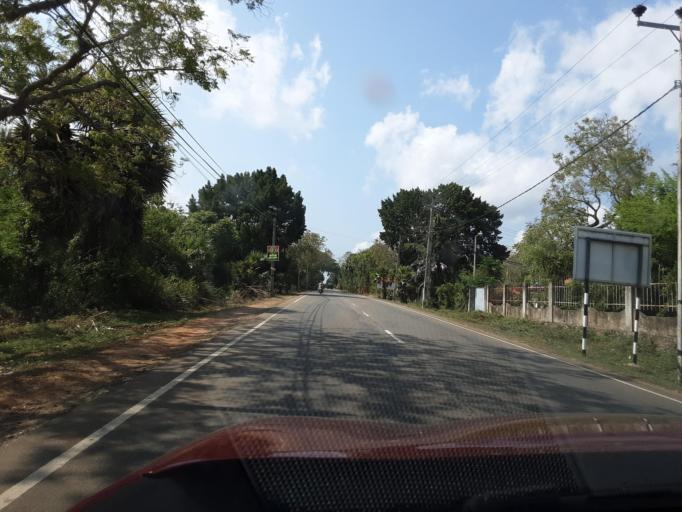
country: LK
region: Southern
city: Tangalla
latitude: 6.2574
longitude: 81.2268
